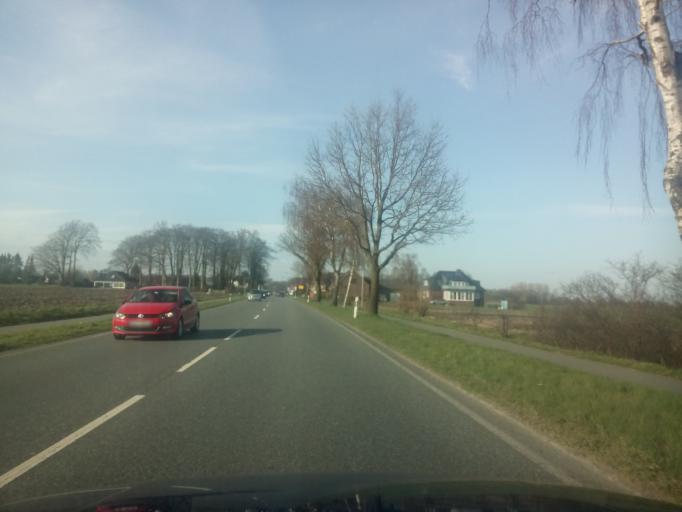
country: DE
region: Lower Saxony
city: Ritterhude
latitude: 53.1974
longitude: 8.7541
